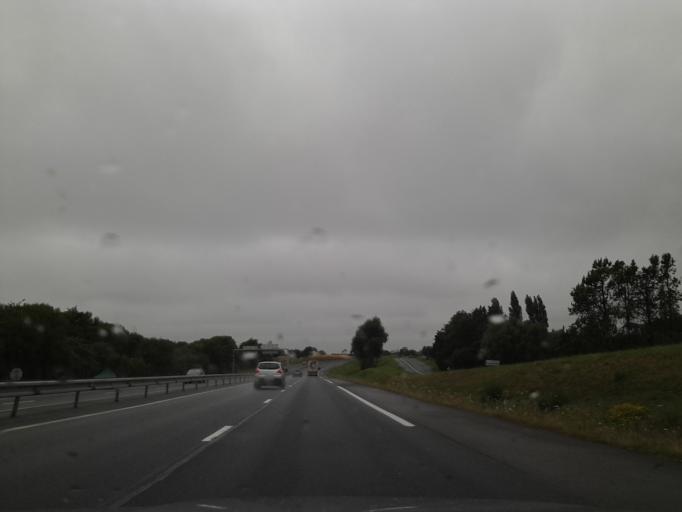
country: FR
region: Lower Normandy
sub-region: Departement de la Manche
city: Sainte-Mere-Eglise
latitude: 49.4034
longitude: -1.3137
